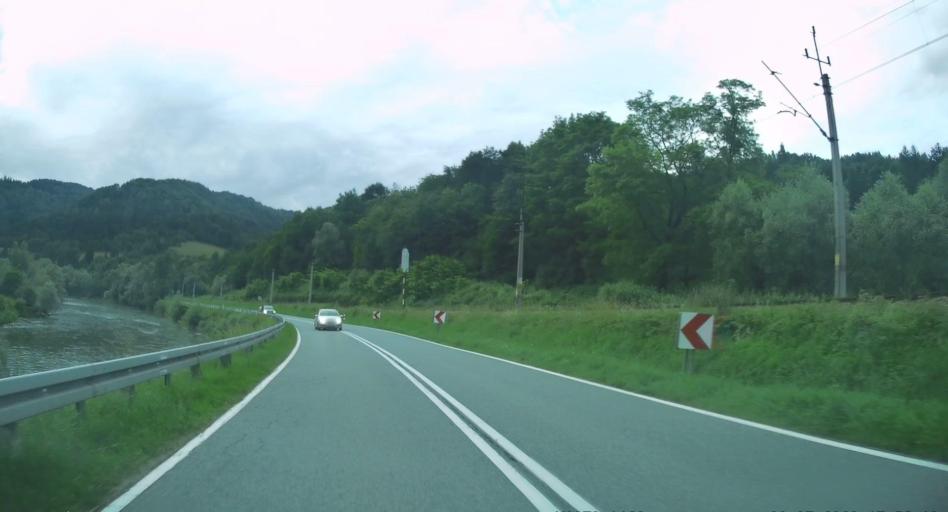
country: PL
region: Lesser Poland Voivodeship
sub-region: Powiat nowosadecki
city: Piwniczna-Zdroj
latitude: 49.3721
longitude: 20.7888
